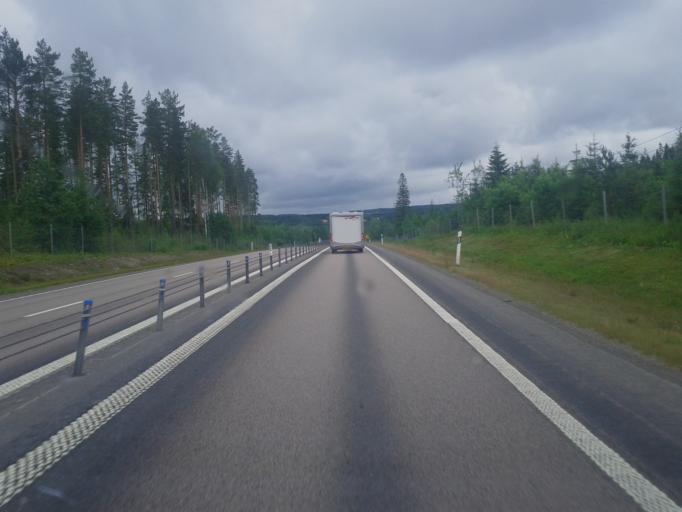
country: SE
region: Vaesternorrland
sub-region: Haernoesands Kommun
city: Haernoesand
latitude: 62.5768
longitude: 17.7541
